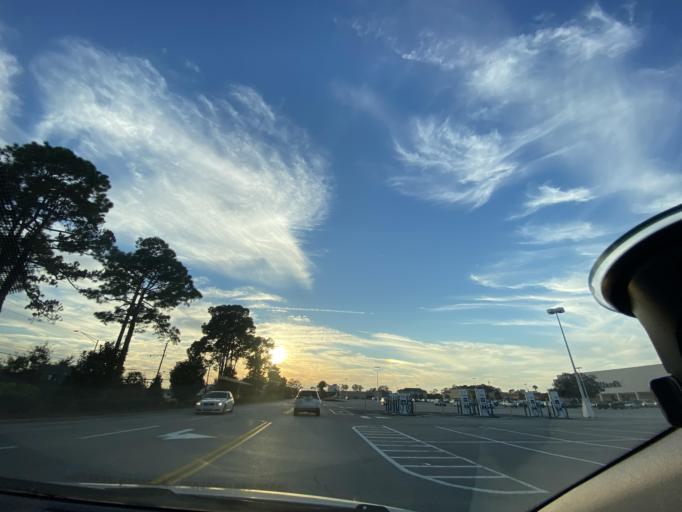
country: US
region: Florida
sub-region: Volusia County
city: Daytona Beach
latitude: 29.1955
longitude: -81.0616
